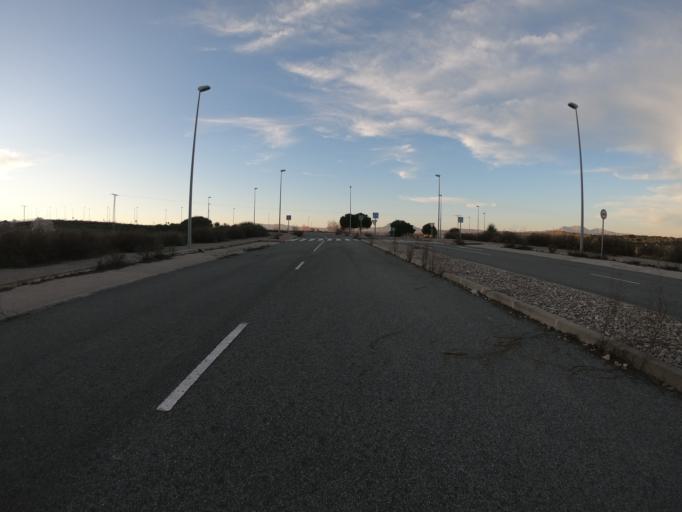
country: ES
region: Basque Country
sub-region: Provincia de Alava
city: Oyon
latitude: 42.4855
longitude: -2.4157
